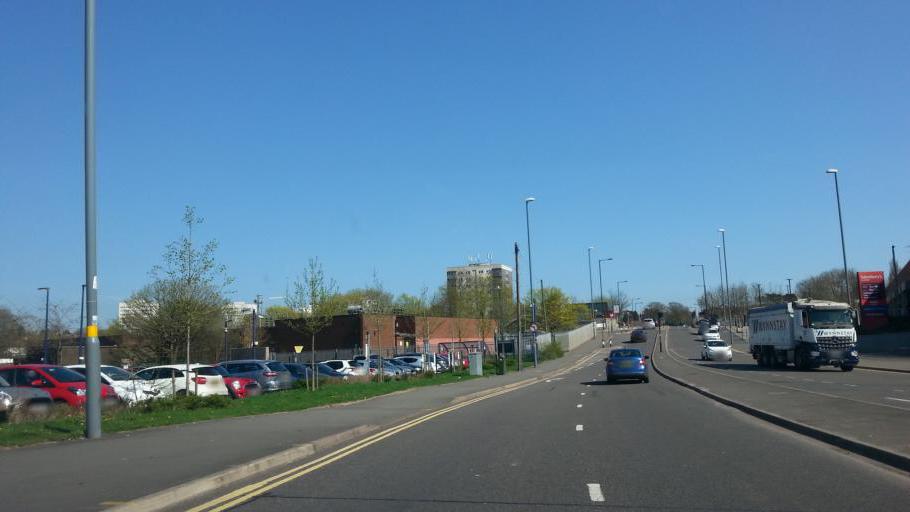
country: GB
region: England
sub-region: City and Borough of Birmingham
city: Bartley Green
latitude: 52.3967
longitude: -1.9835
